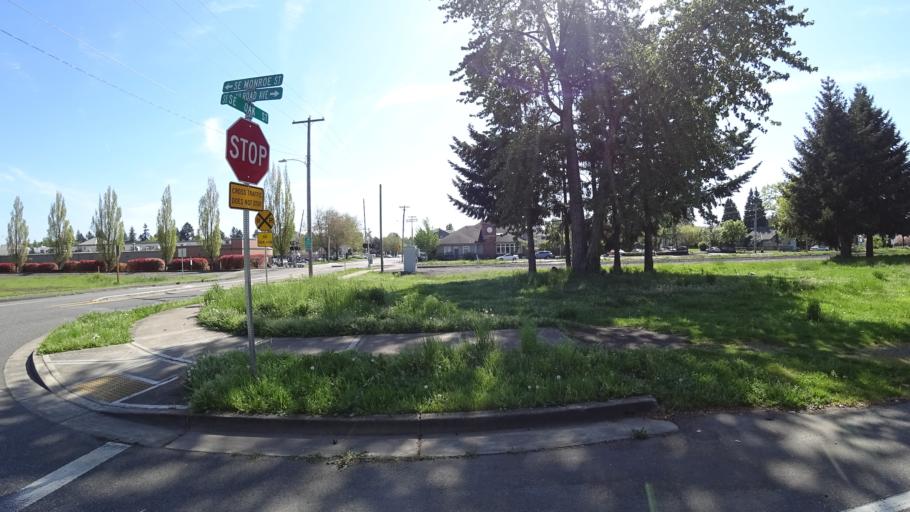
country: US
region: Oregon
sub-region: Clackamas County
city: Milwaukie
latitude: 45.4454
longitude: -122.6281
